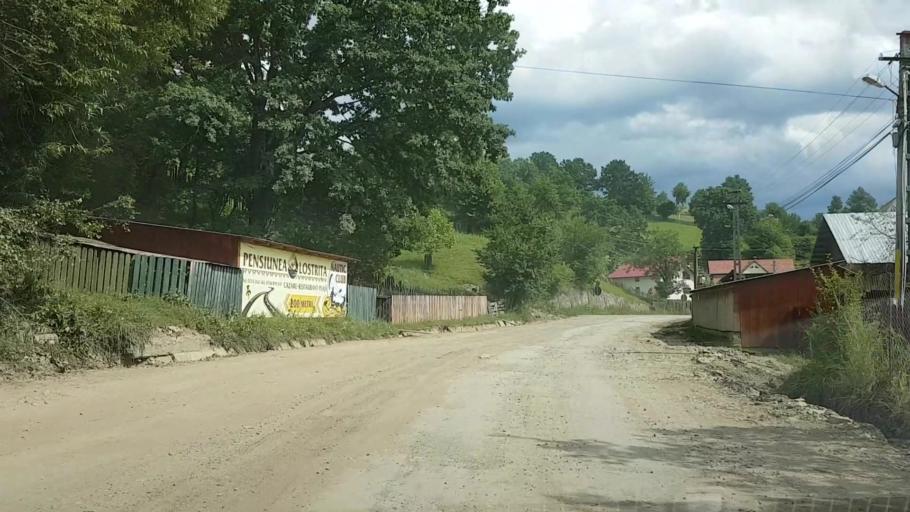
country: RO
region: Neamt
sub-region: Comuna Hangu
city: Hangu
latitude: 47.0234
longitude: 26.0745
